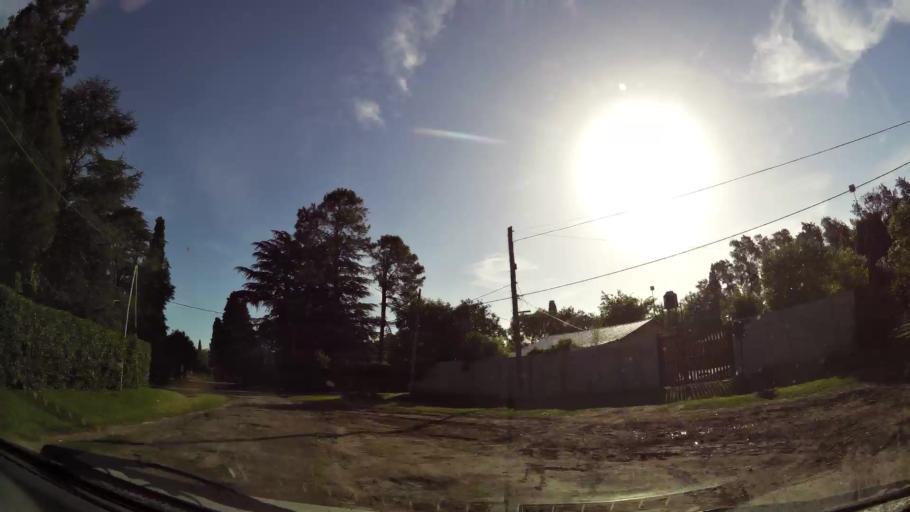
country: AR
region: Buenos Aires
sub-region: Partido de Quilmes
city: Quilmes
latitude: -34.8162
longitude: -58.2170
